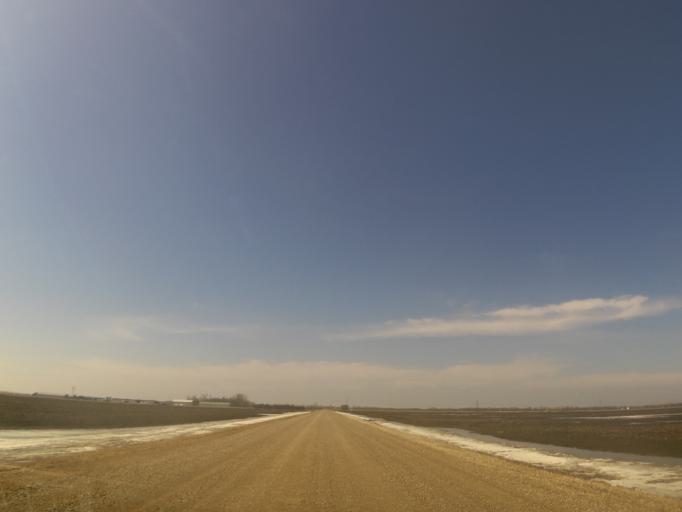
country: US
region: North Dakota
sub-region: Walsh County
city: Grafton
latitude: 48.4265
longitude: -97.2565
